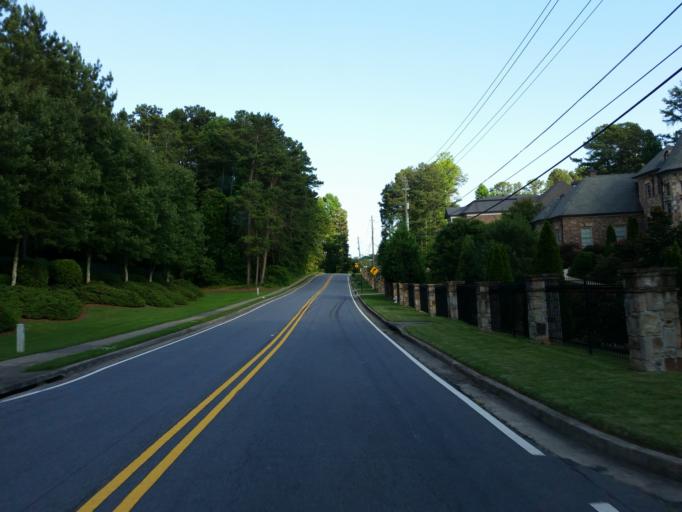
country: US
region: Georgia
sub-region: Cherokee County
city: Woodstock
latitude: 34.0453
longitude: -84.4836
